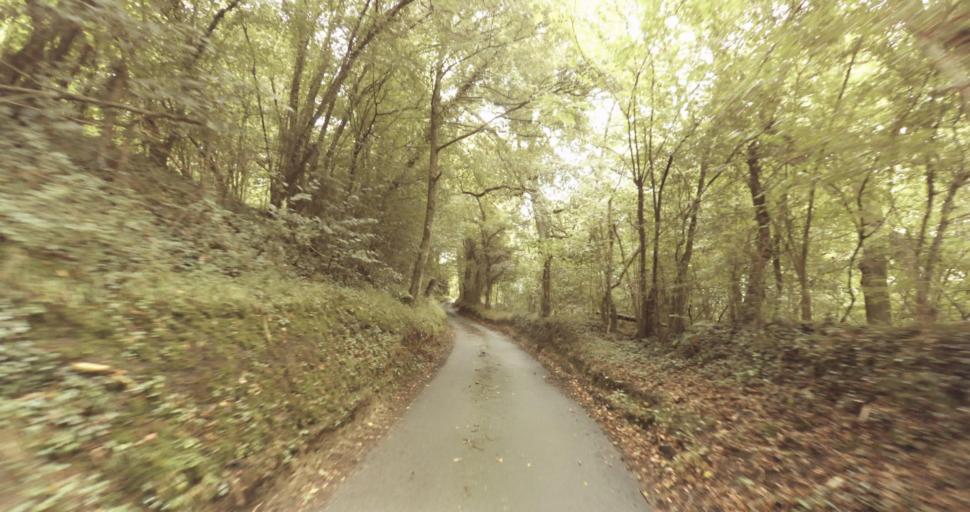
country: FR
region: Lower Normandy
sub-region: Departement de l'Orne
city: Vimoutiers
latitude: 48.8664
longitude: 0.2105
